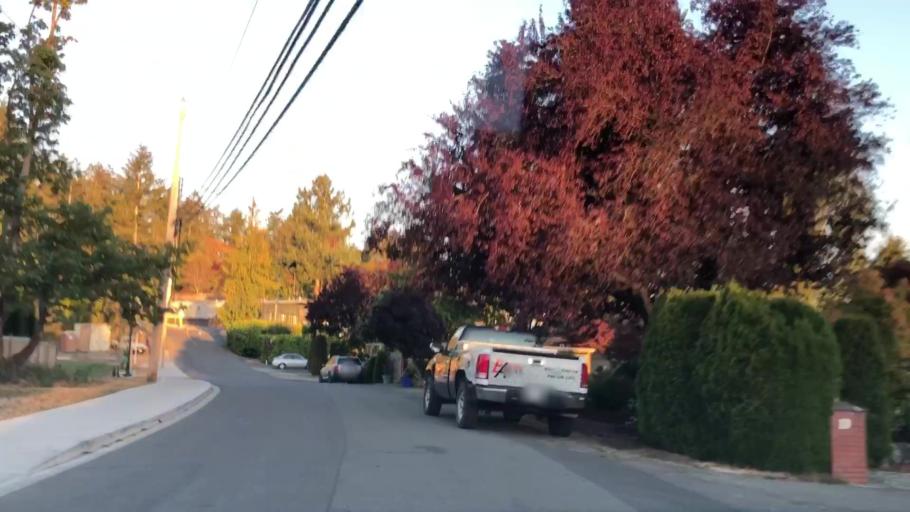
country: CA
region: British Columbia
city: Colwood
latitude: 48.4580
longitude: -123.4415
